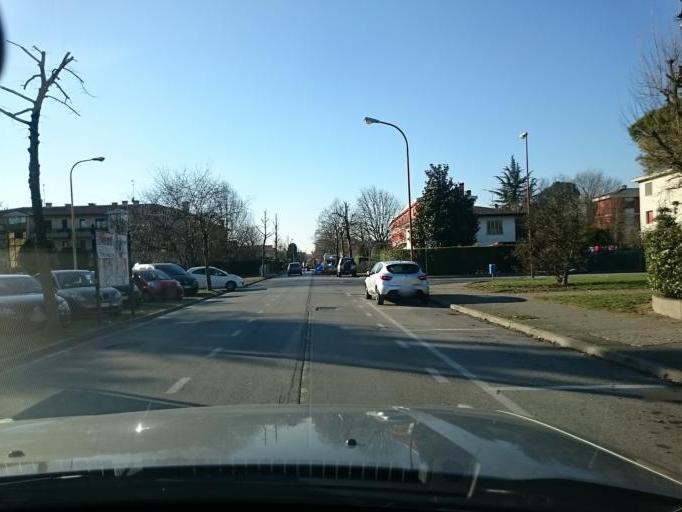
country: IT
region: Veneto
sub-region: Provincia di Venezia
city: Mira Taglio
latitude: 45.4329
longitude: 12.1423
